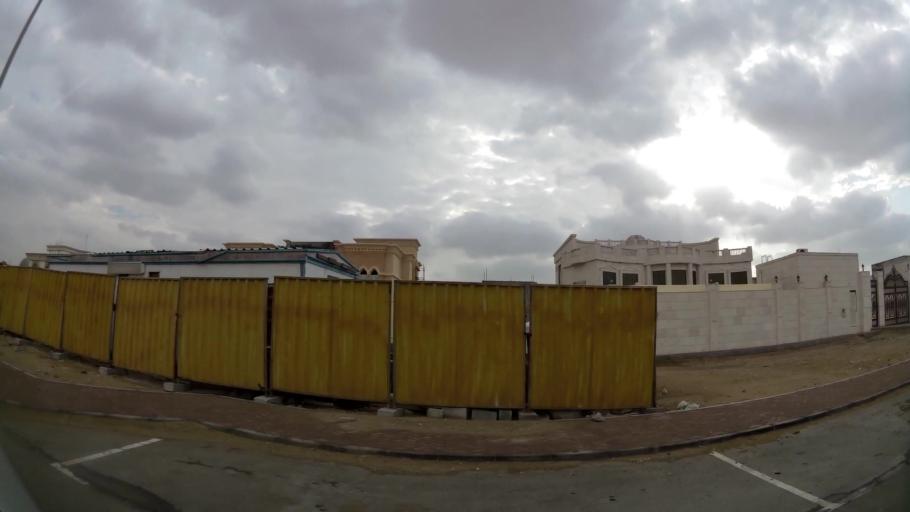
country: AE
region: Abu Dhabi
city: Abu Dhabi
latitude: 24.3496
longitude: 54.6118
